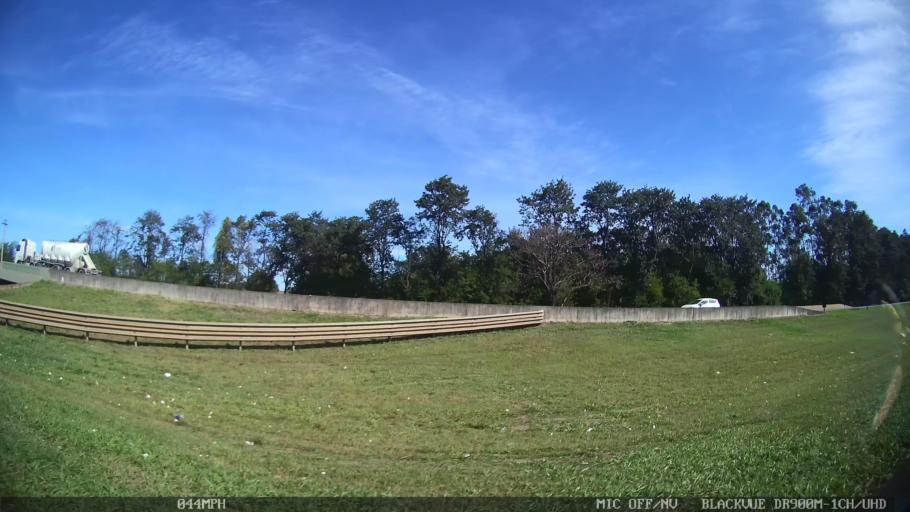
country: BR
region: Sao Paulo
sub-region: Leme
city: Leme
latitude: -22.2457
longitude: -47.3903
